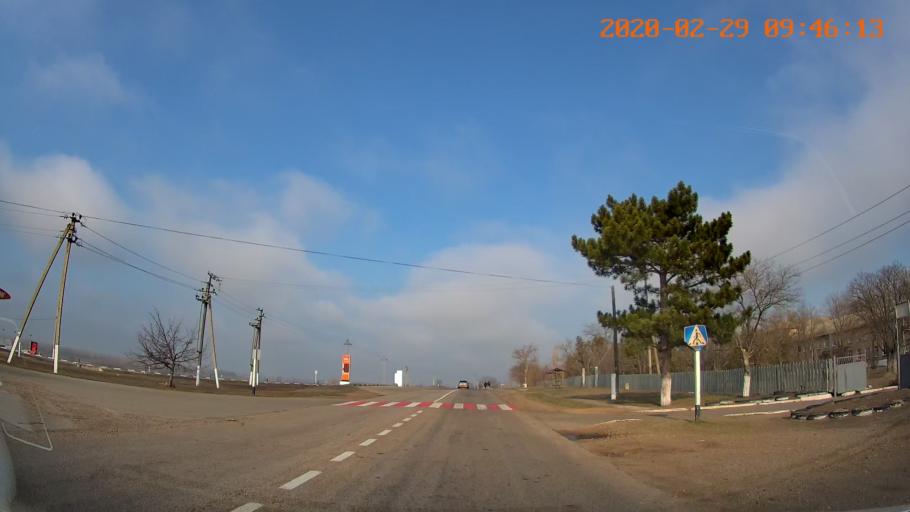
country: MD
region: Telenesti
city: Crasnoe
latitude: 46.6650
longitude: 29.8009
